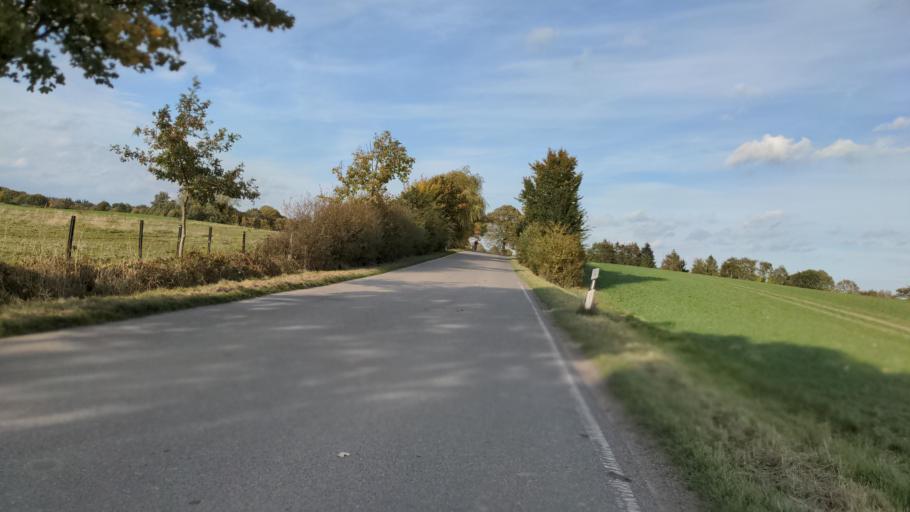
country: DE
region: Schleswig-Holstein
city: Ahrensbok
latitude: 53.9672
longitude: 10.5347
